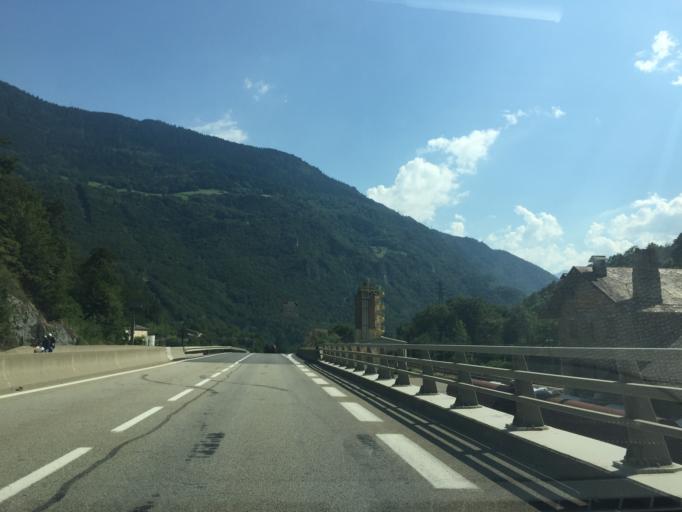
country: FR
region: Rhone-Alpes
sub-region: Departement de la Savoie
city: Moutiers
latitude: 45.5053
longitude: 6.5633
